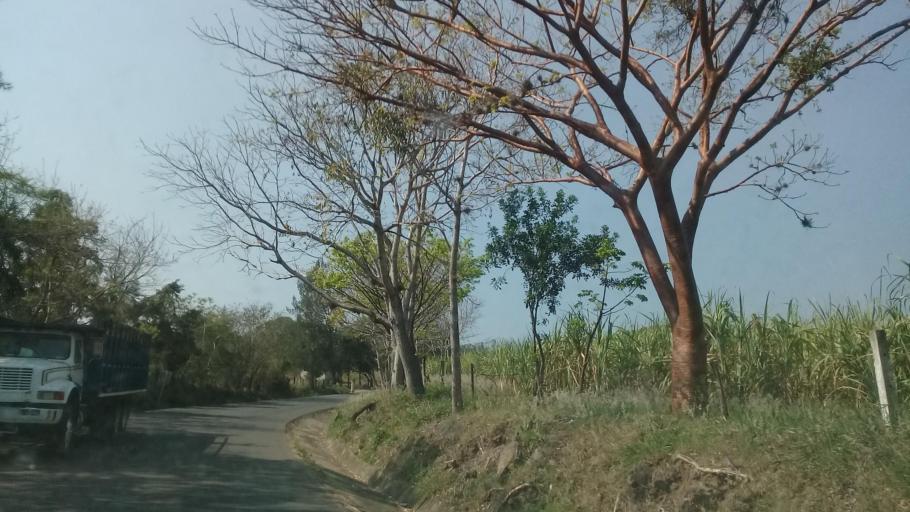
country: MX
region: Veracruz
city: El Castillo
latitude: 19.5795
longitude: -96.8294
